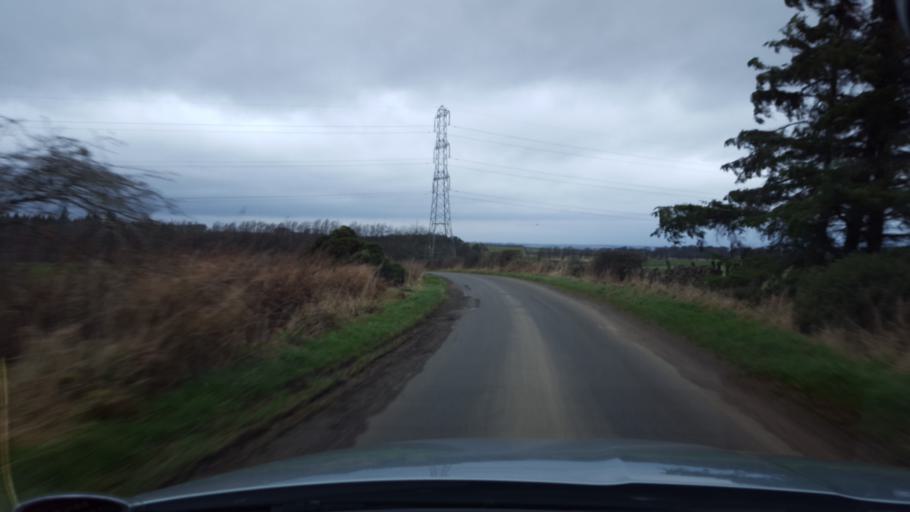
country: GB
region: Scotland
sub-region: West Lothian
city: Kirknewton
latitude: 55.8694
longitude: -3.4352
